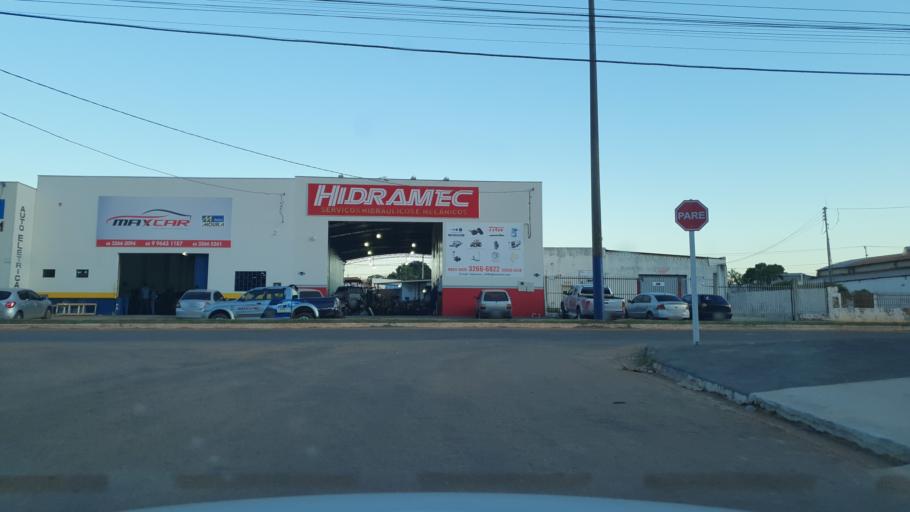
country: BR
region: Mato Grosso
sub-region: Pontes E Lacerda
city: Pontes e Lacerda
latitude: -15.2261
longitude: -59.3225
